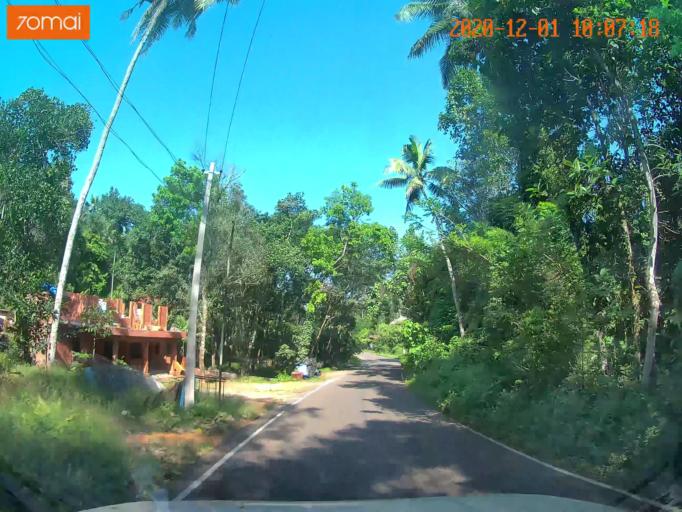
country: IN
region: Kerala
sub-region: Ernakulam
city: Piravam
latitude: 9.8142
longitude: 76.5603
